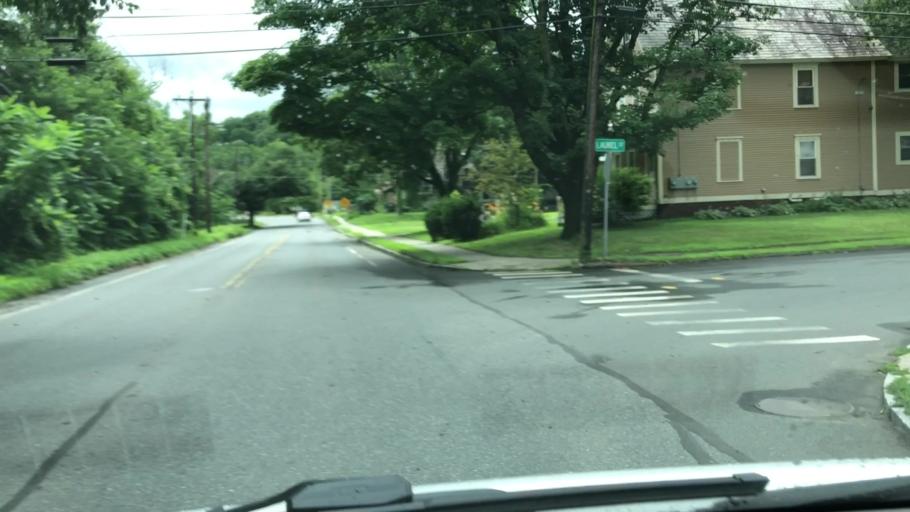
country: US
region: Massachusetts
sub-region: Franklin County
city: Greenfield
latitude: 42.5844
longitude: -72.6120
